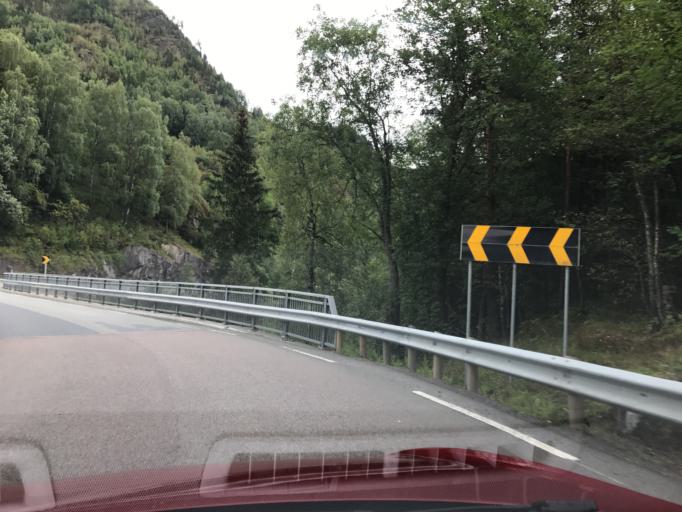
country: NO
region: Buskerud
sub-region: Nore og Uvdal
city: Rodberg
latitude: 60.2619
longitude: 8.9821
